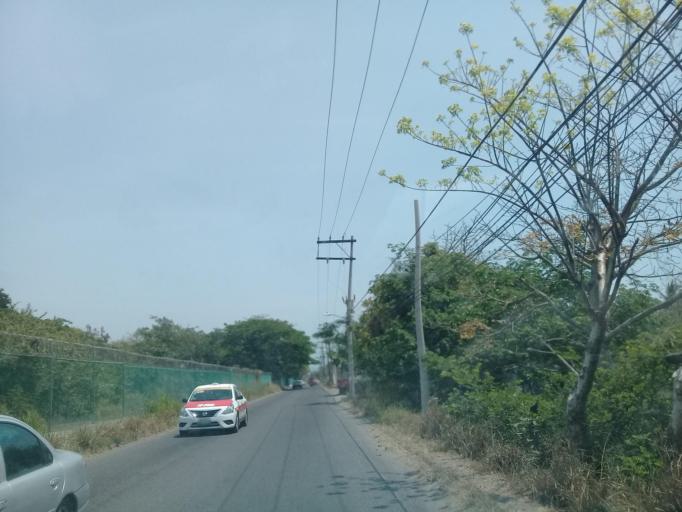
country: MX
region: Veracruz
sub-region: Veracruz
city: Hacienda Sotavento
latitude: 19.1402
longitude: -96.1778
